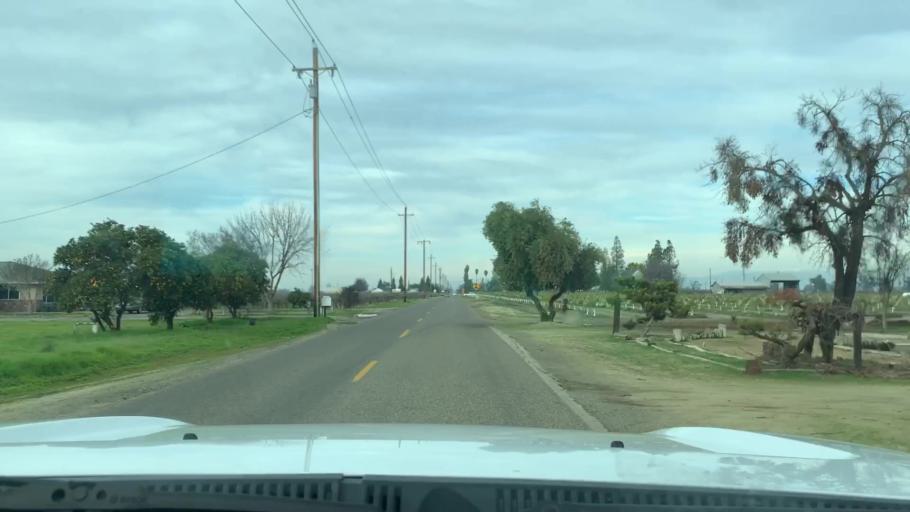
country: US
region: California
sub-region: Fresno County
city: Selma
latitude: 36.5589
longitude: -119.5750
